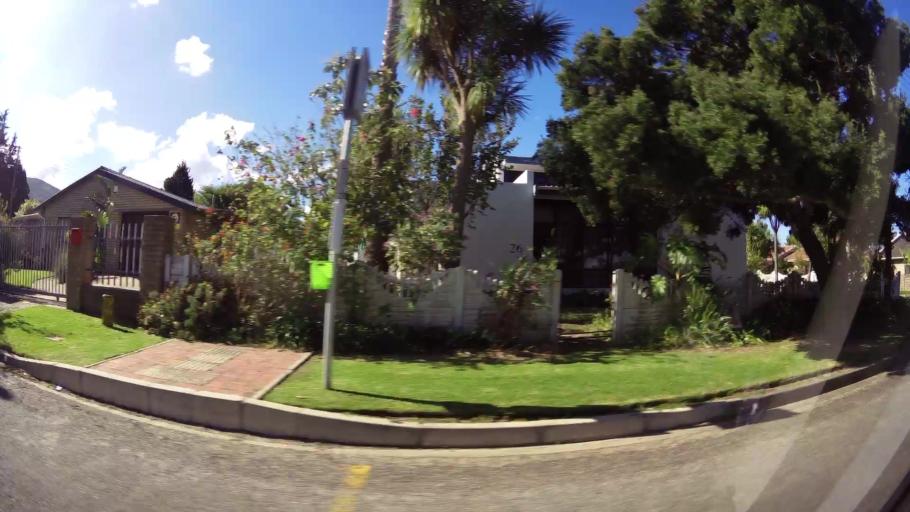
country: ZA
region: Western Cape
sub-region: Eden District Municipality
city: George
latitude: -33.9403
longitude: 22.4718
